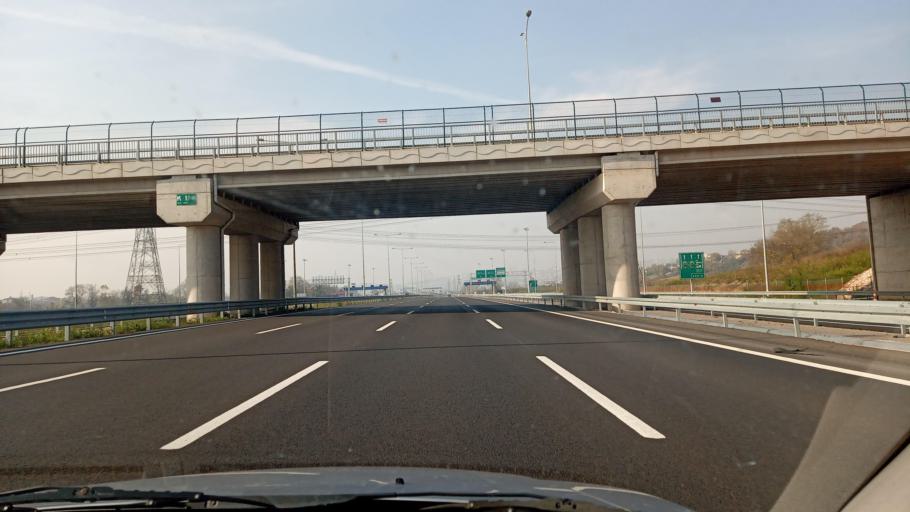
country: TR
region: Sakarya
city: Kazimpasa
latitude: 40.8420
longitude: 30.3472
